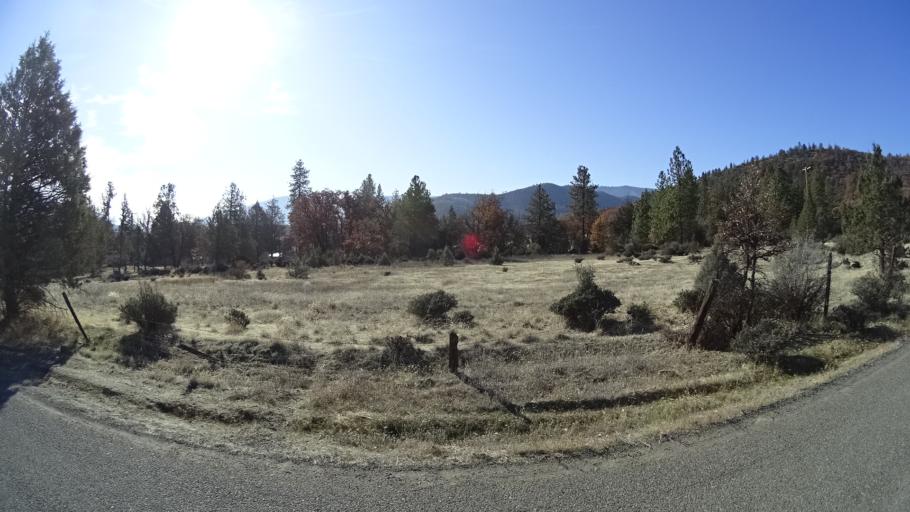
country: US
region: California
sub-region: Siskiyou County
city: Yreka
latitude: 41.6996
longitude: -122.6494
